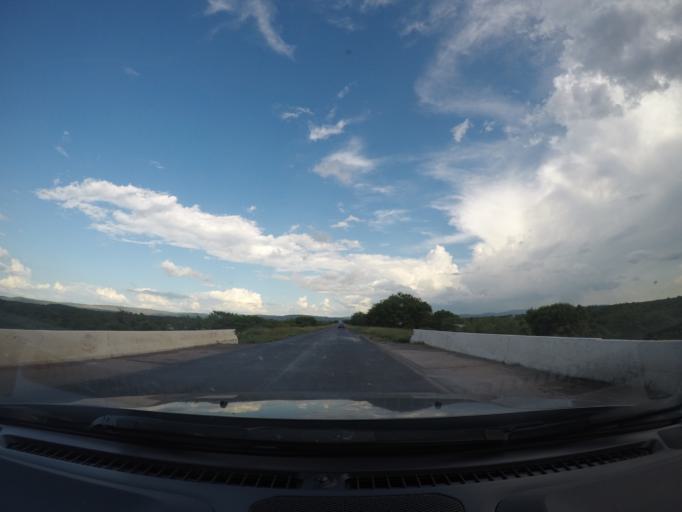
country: BR
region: Bahia
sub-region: Ibotirama
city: Ibotirama
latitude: -12.1706
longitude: -43.2648
